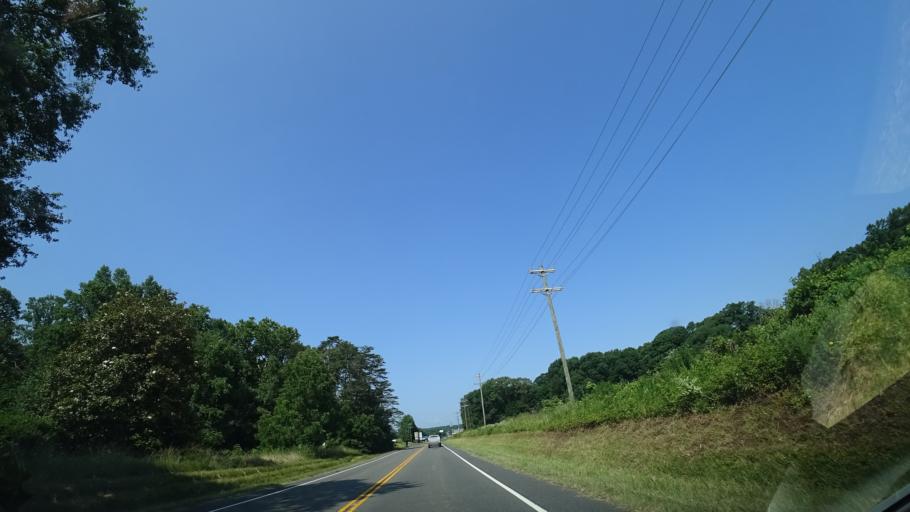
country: US
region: Virginia
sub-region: Louisa County
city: Louisa
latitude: 38.0906
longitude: -77.8046
